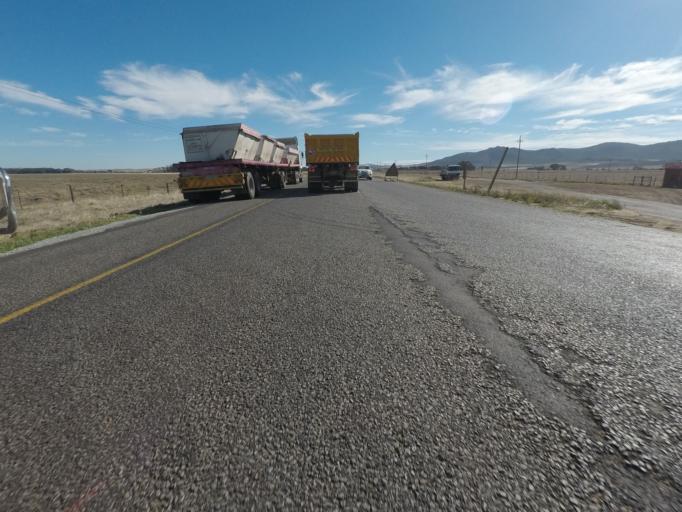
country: ZA
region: Western Cape
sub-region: West Coast District Municipality
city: Malmesbury
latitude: -33.6274
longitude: 18.7236
